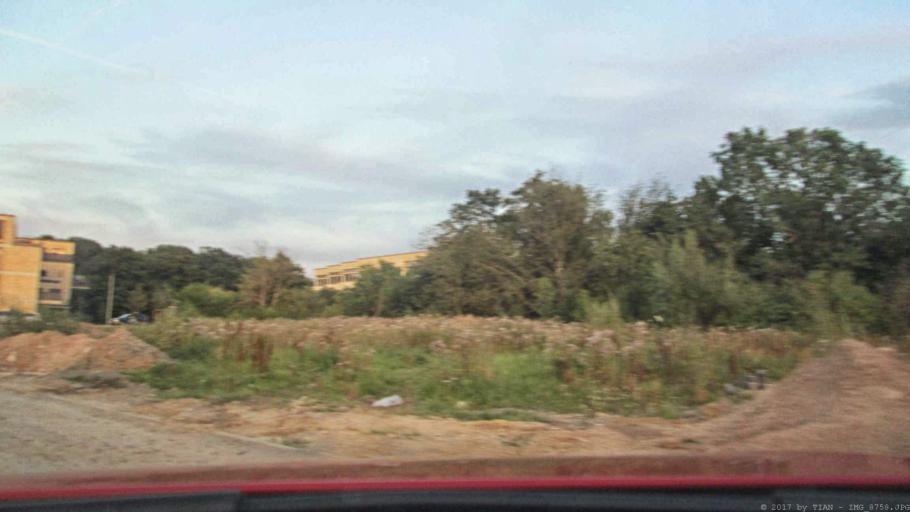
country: DE
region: Lower Saxony
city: Wolfsburg
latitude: 52.4045
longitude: 10.7470
